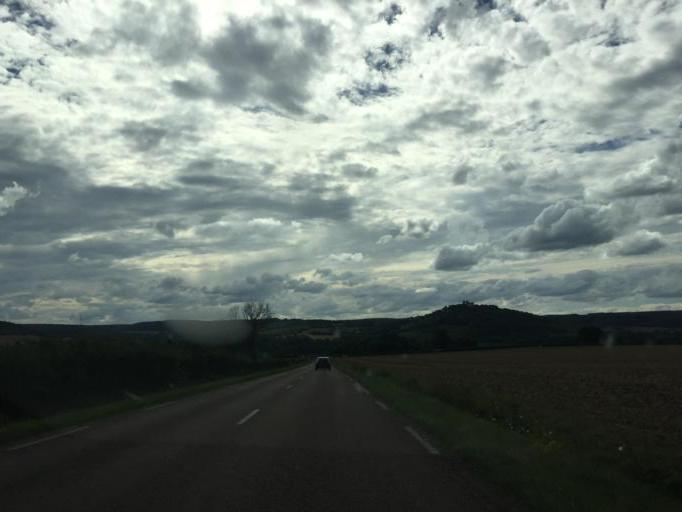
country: FR
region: Bourgogne
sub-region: Departement de l'Yonne
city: Avallon
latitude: 47.4655
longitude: 3.7826
